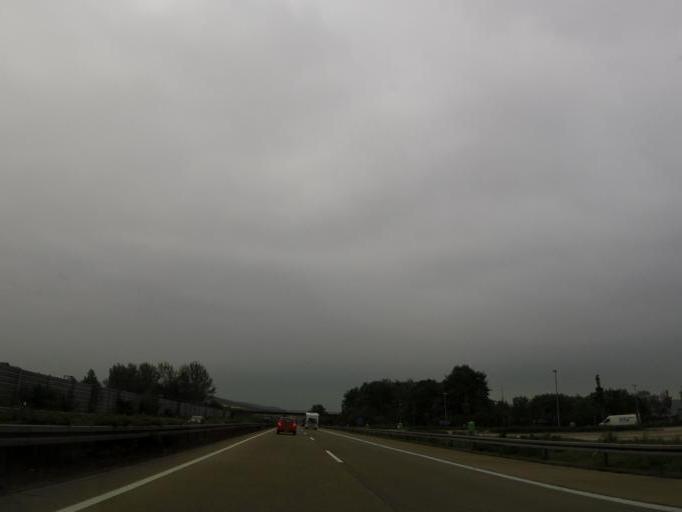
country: DE
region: Lower Saxony
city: Seesen
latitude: 51.8562
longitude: 10.1247
